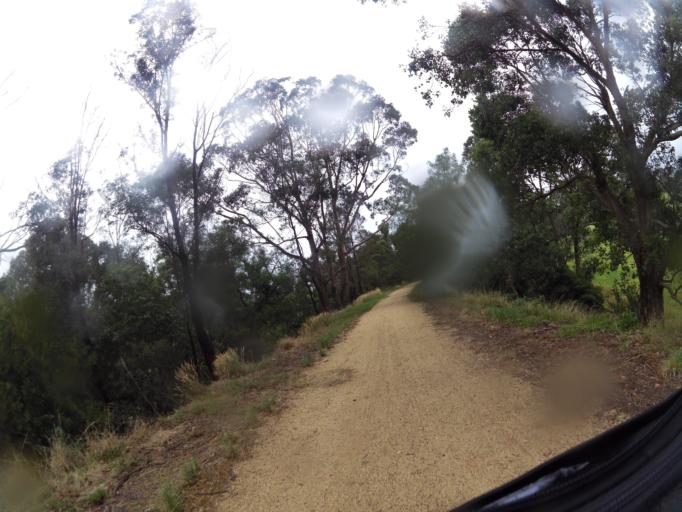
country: AU
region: Victoria
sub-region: East Gippsland
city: Lakes Entrance
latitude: -37.7638
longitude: 147.8212
